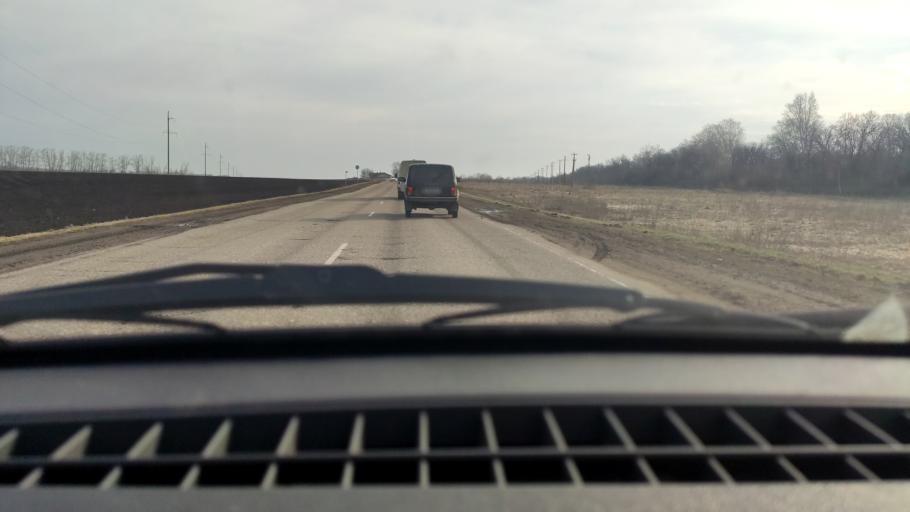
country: RU
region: Bashkortostan
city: Chishmy
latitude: 54.5459
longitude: 55.3249
